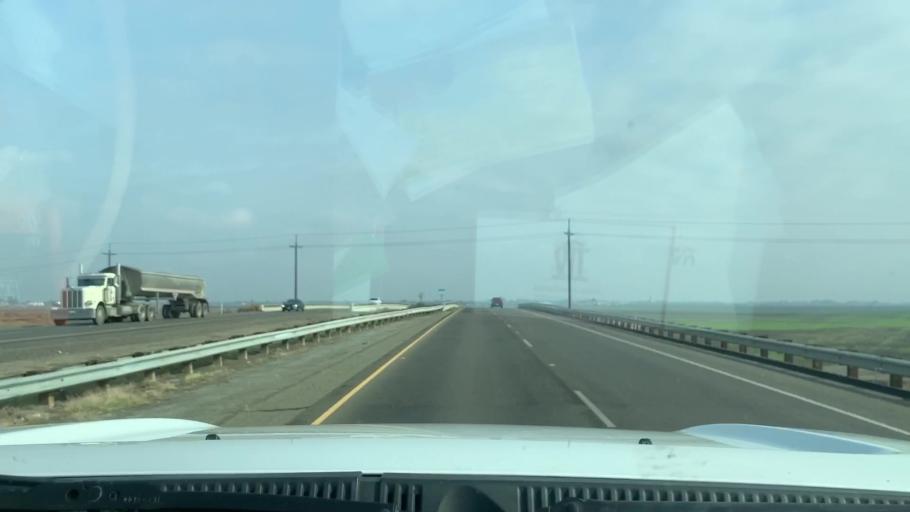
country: US
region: California
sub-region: Kings County
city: Lemoore
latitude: 36.2701
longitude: -119.8359
